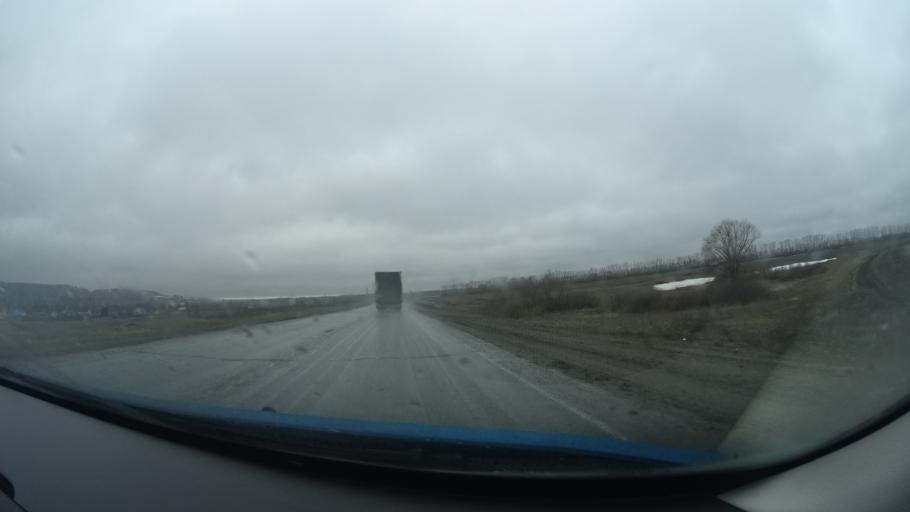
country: RU
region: Bashkortostan
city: Kandry
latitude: 54.5732
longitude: 54.2281
